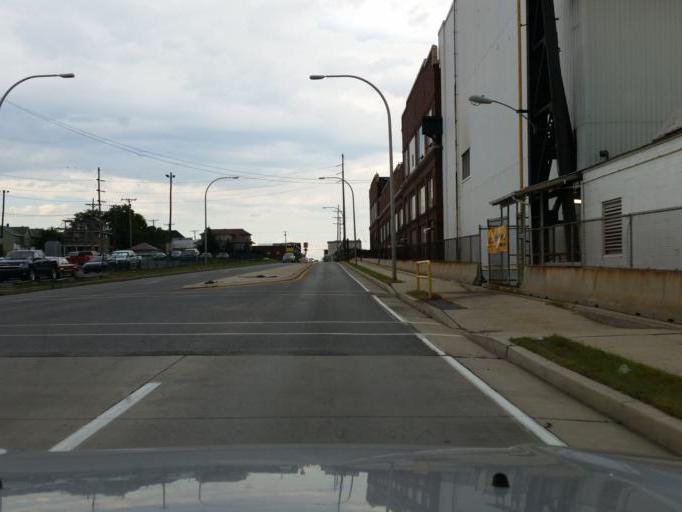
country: US
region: Pennsylvania
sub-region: Blair County
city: Altoona
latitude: 40.5351
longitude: -78.3841
